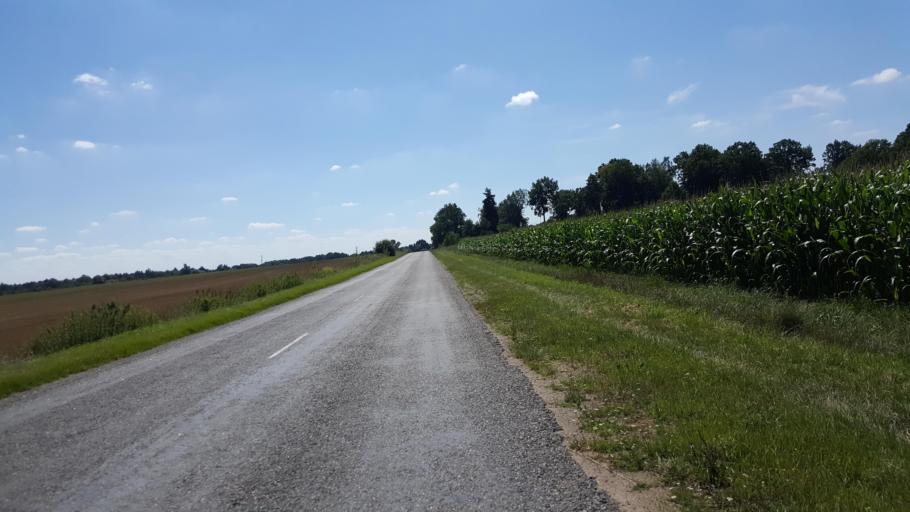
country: BY
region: Brest
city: Charnawchytsy
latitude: 52.3346
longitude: 23.6059
